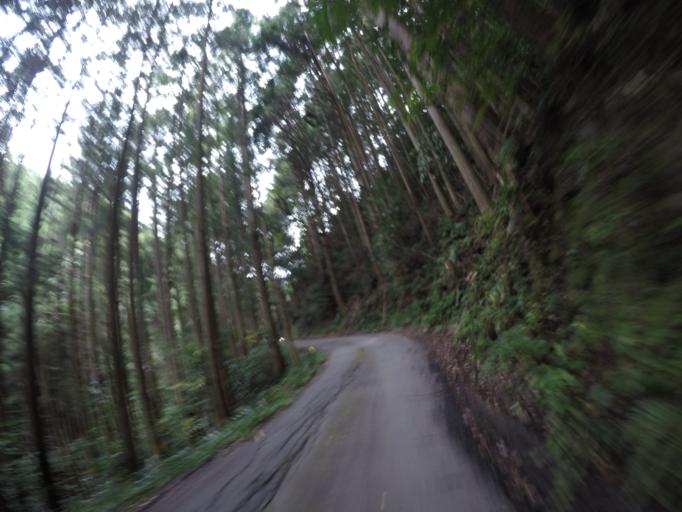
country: JP
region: Shizuoka
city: Shimada
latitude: 34.8835
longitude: 138.1698
